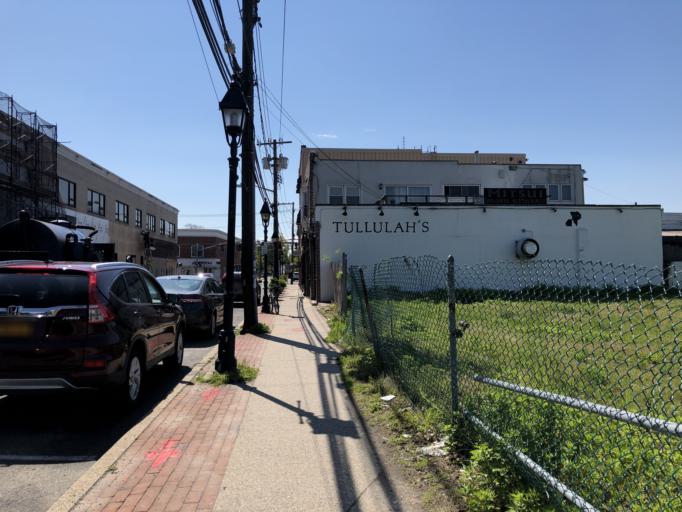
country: US
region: New York
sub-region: Suffolk County
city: Bay Shore
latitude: 40.7220
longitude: -73.2486
